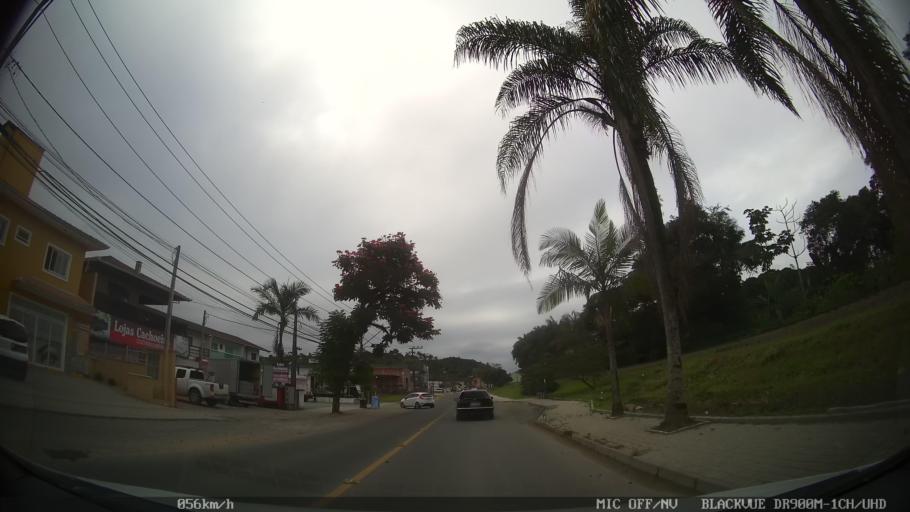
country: BR
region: Santa Catarina
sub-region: Joinville
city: Joinville
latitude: -26.3361
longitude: -48.8783
